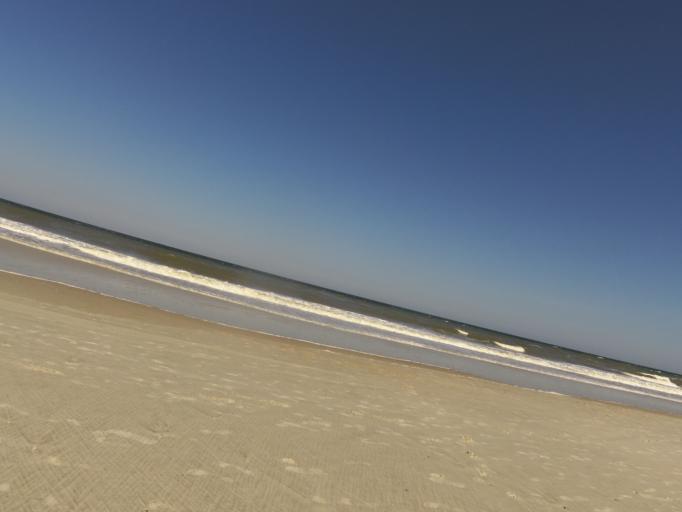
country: US
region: Florida
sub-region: Duval County
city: Atlantic Beach
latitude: 30.3527
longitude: -81.3967
